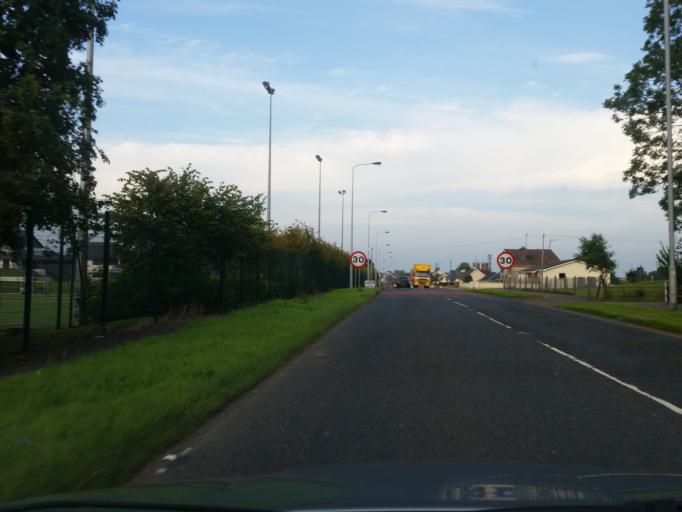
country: GB
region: Northern Ireland
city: Fivemiletown
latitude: 54.3741
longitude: -7.3262
